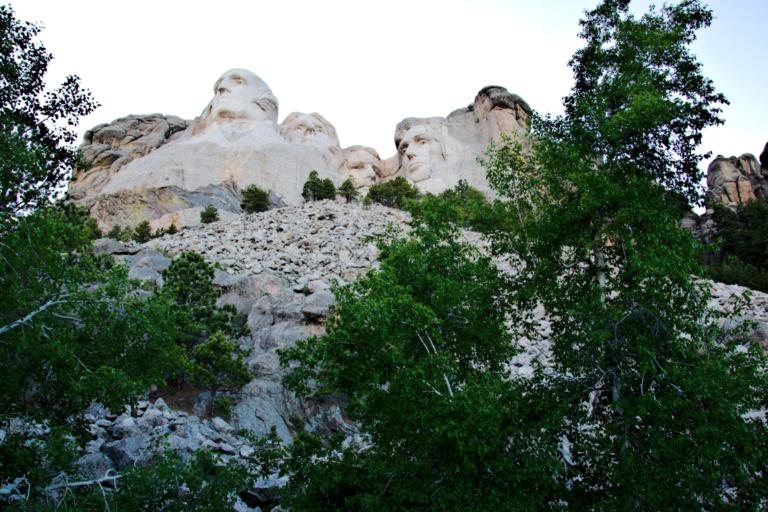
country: US
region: South Dakota
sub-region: Custer County
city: Custer
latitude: 43.8785
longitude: -103.4578
